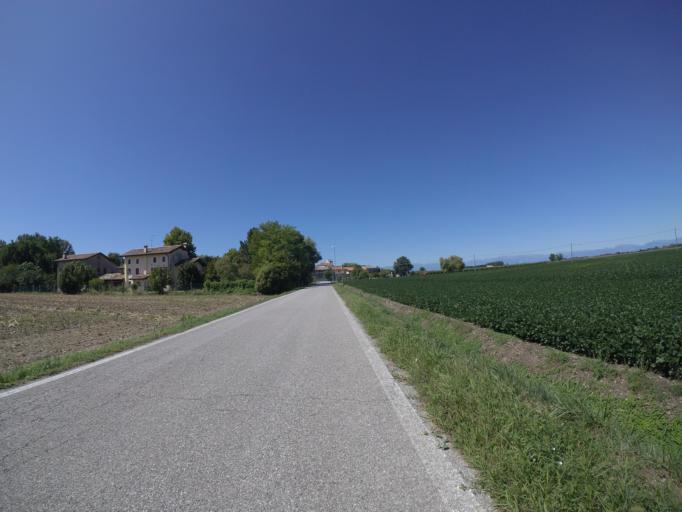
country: IT
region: Friuli Venezia Giulia
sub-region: Provincia di Udine
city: Rivignano
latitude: 45.8601
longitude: 13.0175
